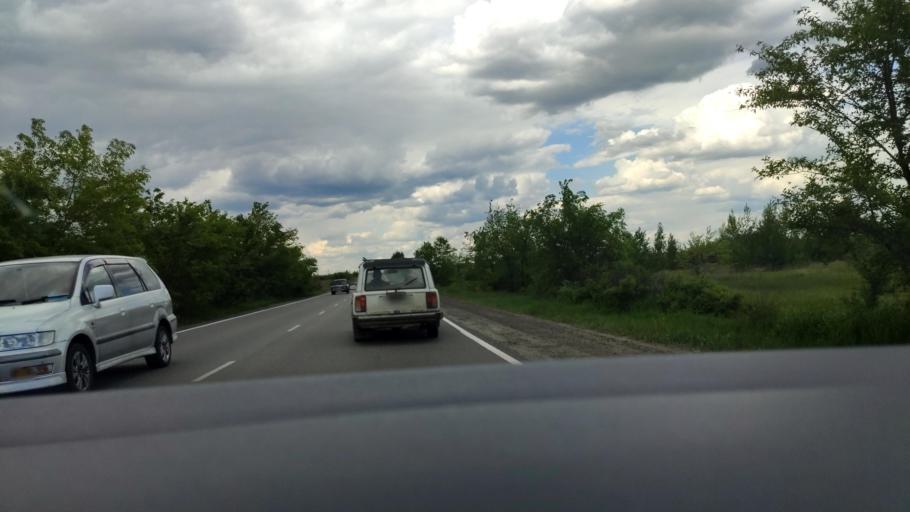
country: RU
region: Voronezj
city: Maslovka
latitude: 51.5637
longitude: 39.2742
